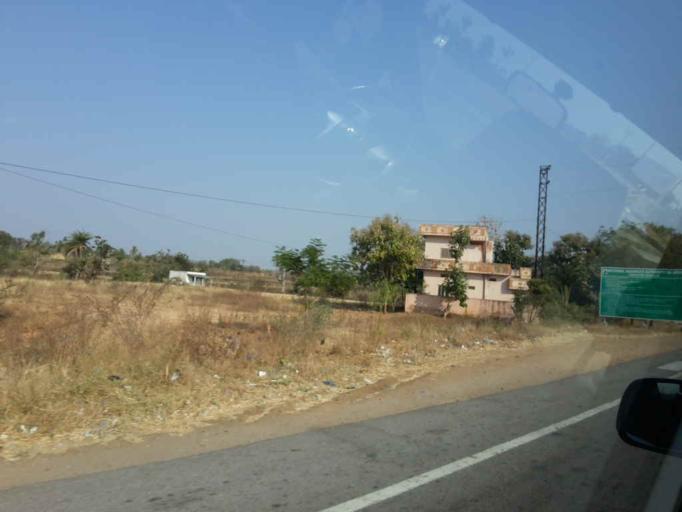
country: IN
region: Telangana
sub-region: Nizamabad District
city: Nizamabad
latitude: 18.5333
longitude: 78.2372
